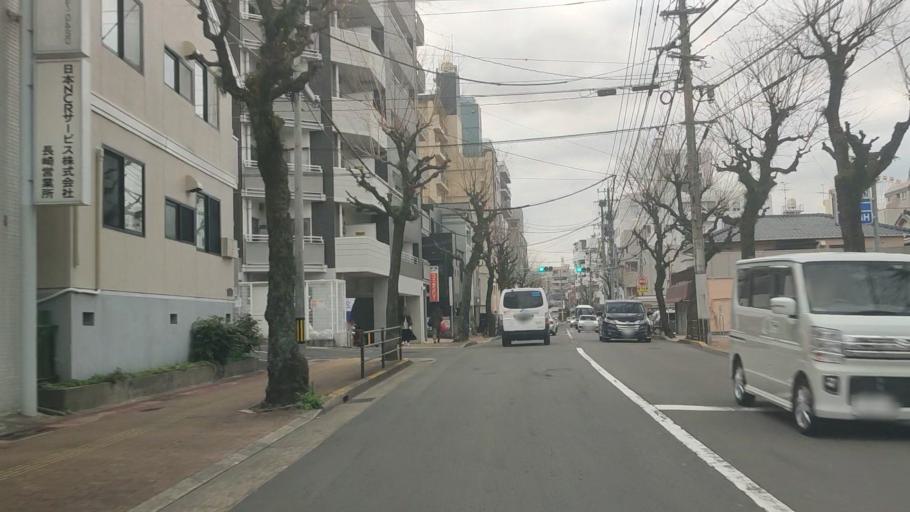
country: JP
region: Nagasaki
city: Nagasaki-shi
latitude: 32.7673
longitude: 129.8668
